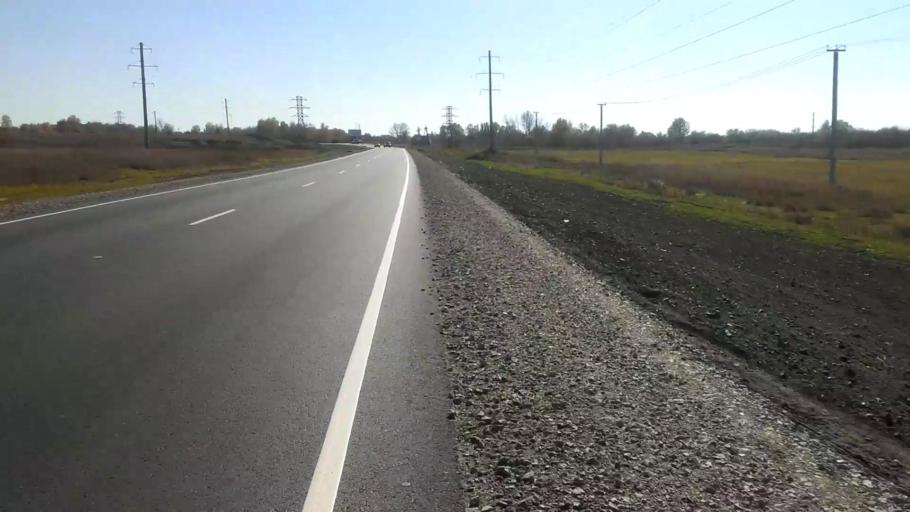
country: RU
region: Altai Krai
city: Sannikovo
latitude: 53.3322
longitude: 83.9380
